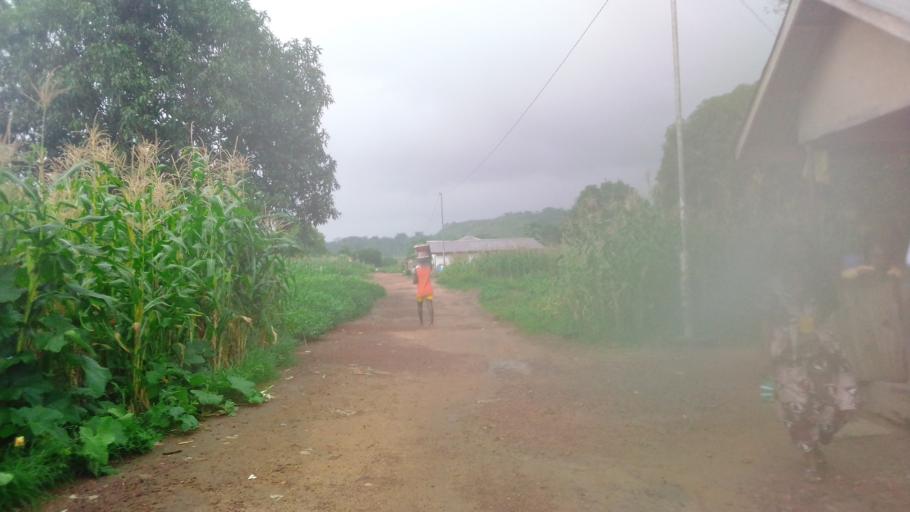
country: SL
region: Northern Province
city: Lunsar
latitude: 8.6844
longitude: -12.5289
